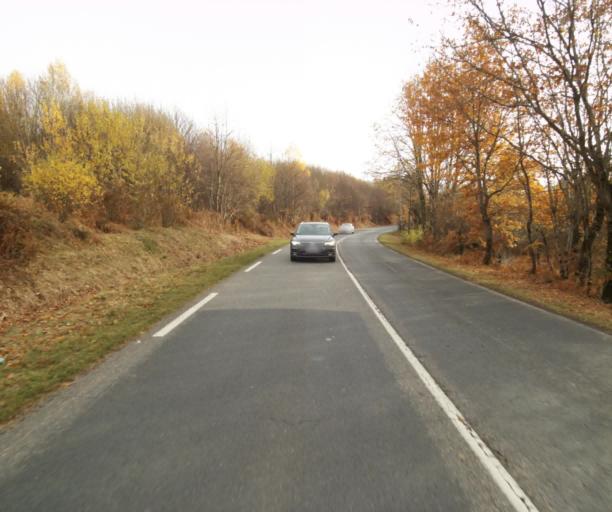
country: FR
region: Limousin
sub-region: Departement de la Correze
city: Sainte-Fortunade
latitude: 45.2001
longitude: 1.7727
